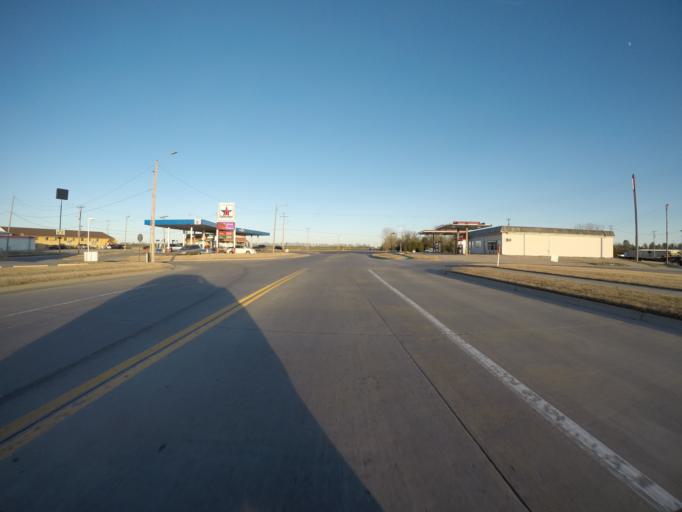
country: US
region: Kansas
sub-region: Harvey County
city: Newton
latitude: 38.0427
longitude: -97.3196
